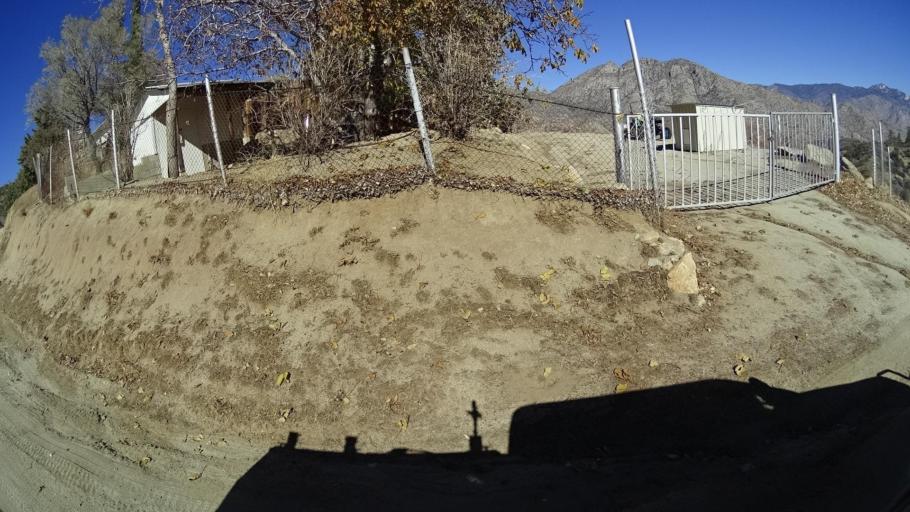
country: US
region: California
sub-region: Kern County
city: Wofford Heights
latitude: 35.7072
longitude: -118.5031
